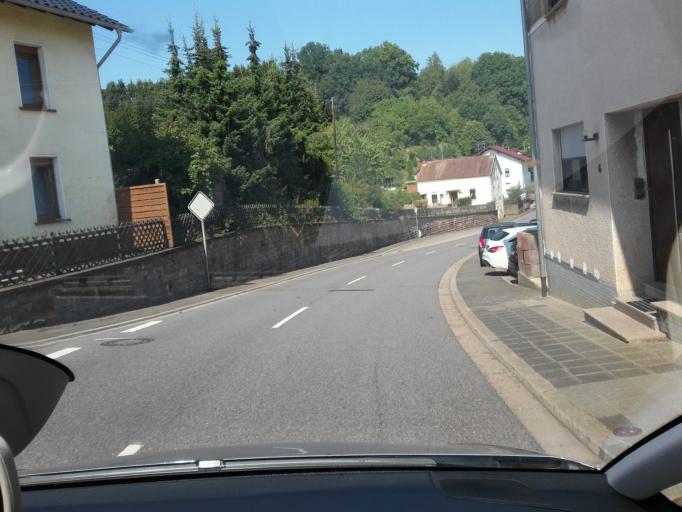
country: DE
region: Saarland
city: Mettlach
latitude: 49.4698
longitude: 6.5888
